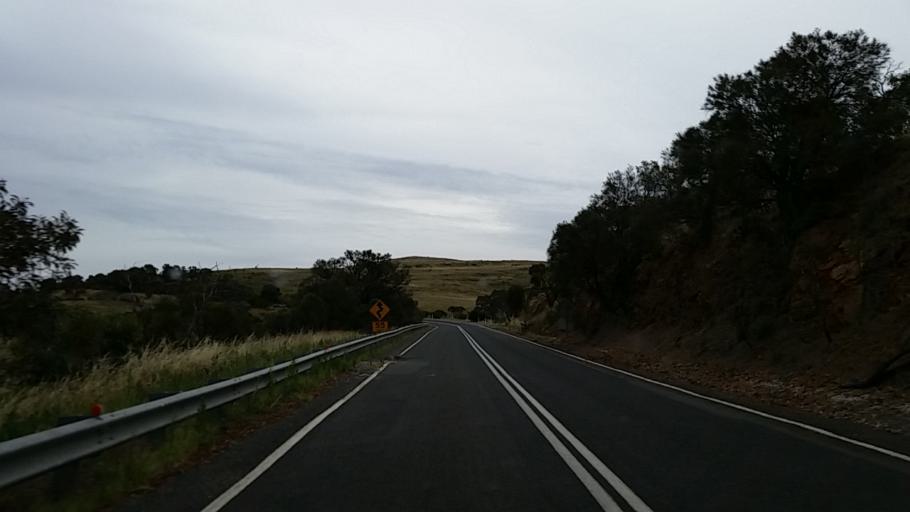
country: AU
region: South Australia
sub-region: Mid Murray
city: Mannum
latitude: -34.7616
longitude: 139.2027
